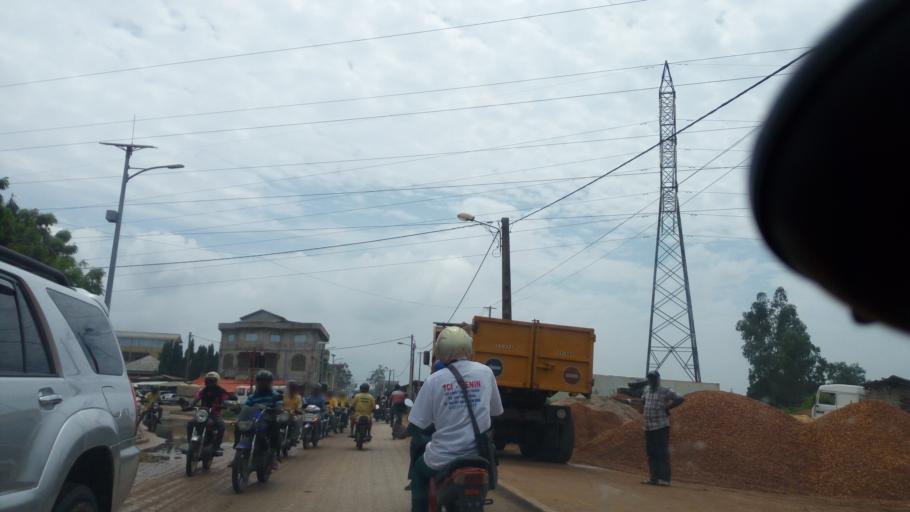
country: BJ
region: Atlantique
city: Abomey-Calavi
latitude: 6.3819
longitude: 2.3413
